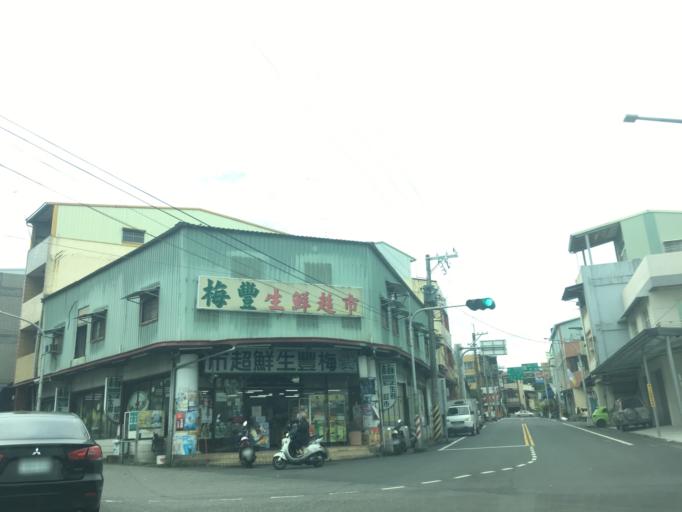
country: TW
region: Taiwan
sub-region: Yunlin
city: Douliu
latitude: 23.5863
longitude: 120.5553
